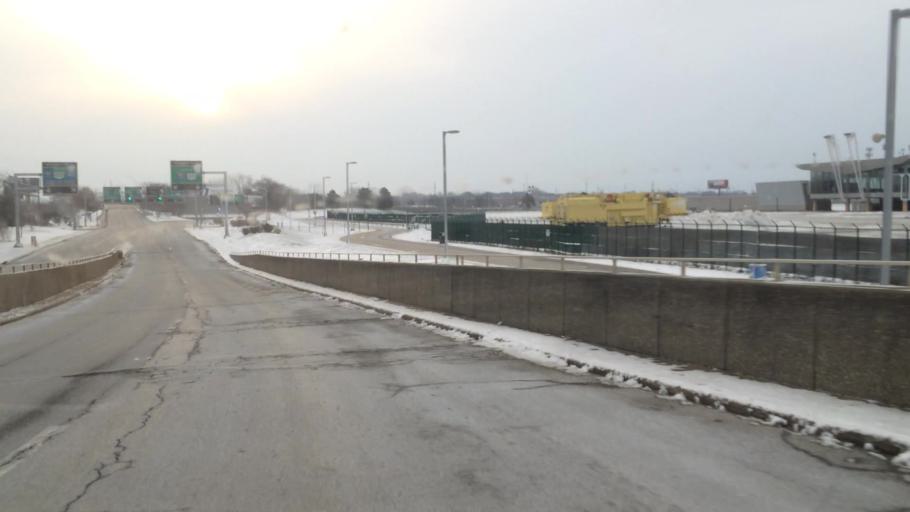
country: US
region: Ohio
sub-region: Cuyahoga County
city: Brook Park
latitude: 41.4094
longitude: -81.8381
